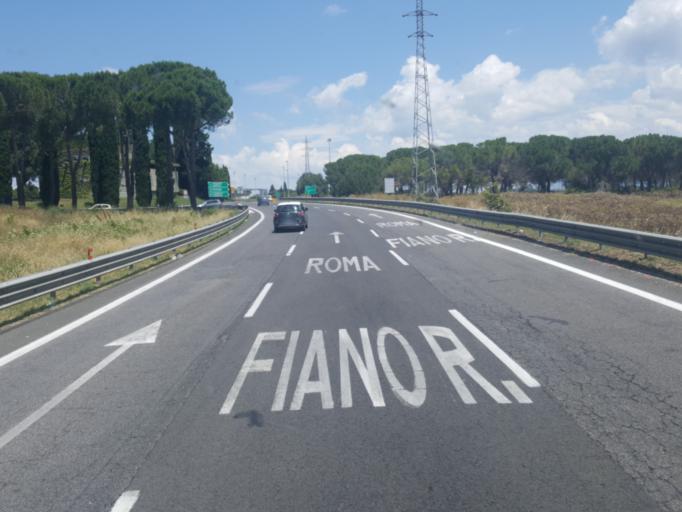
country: IT
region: Latium
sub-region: Citta metropolitana di Roma Capitale
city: Bivio di Capanelle
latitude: 42.1354
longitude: 12.6047
